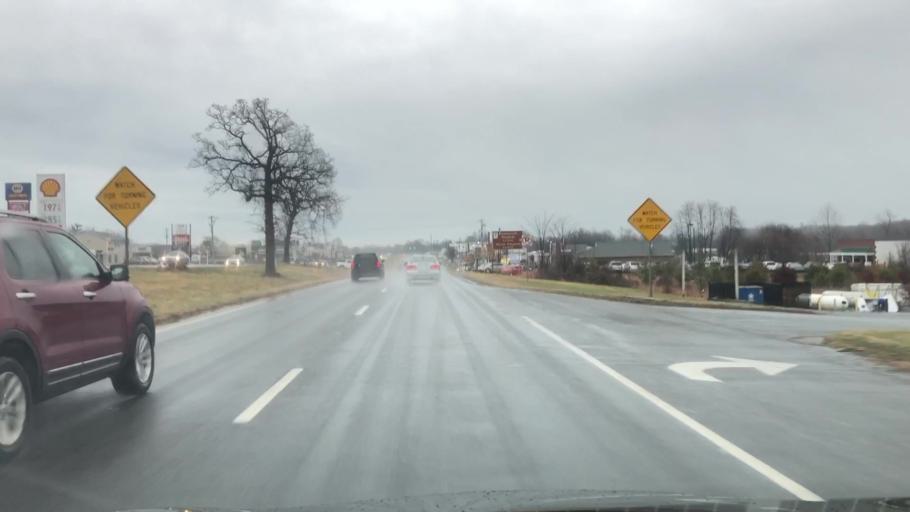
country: US
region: Virginia
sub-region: Greene County
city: Ruckersville
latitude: 38.2284
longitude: -78.3723
